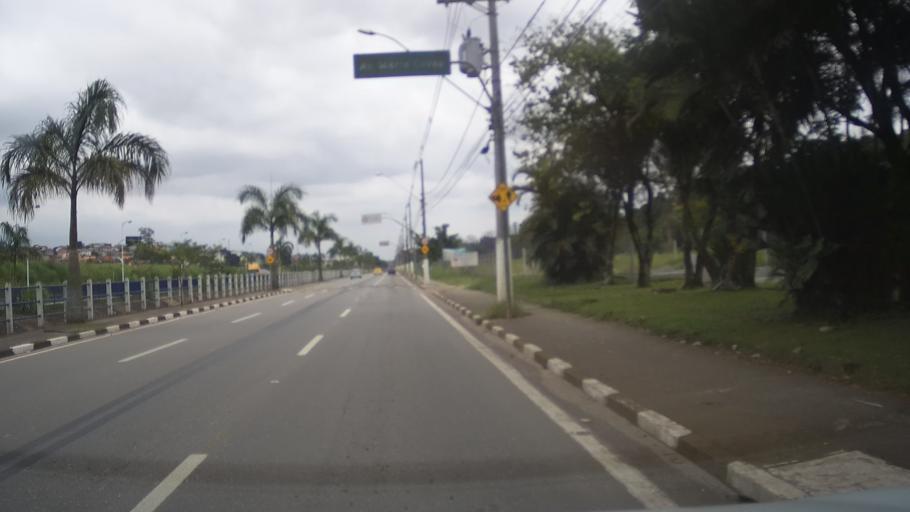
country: BR
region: Sao Paulo
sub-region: Aruja
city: Aruja
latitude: -23.3972
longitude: -46.3348
